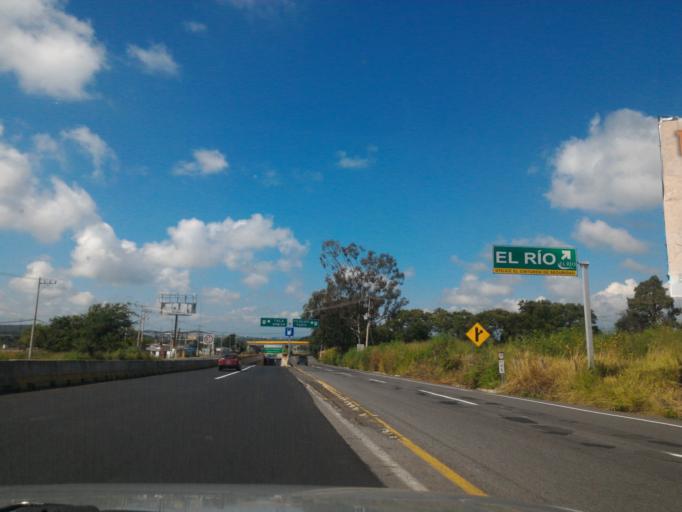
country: MX
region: Jalisco
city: La Venta del Astillero
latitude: 20.7334
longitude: -103.6021
